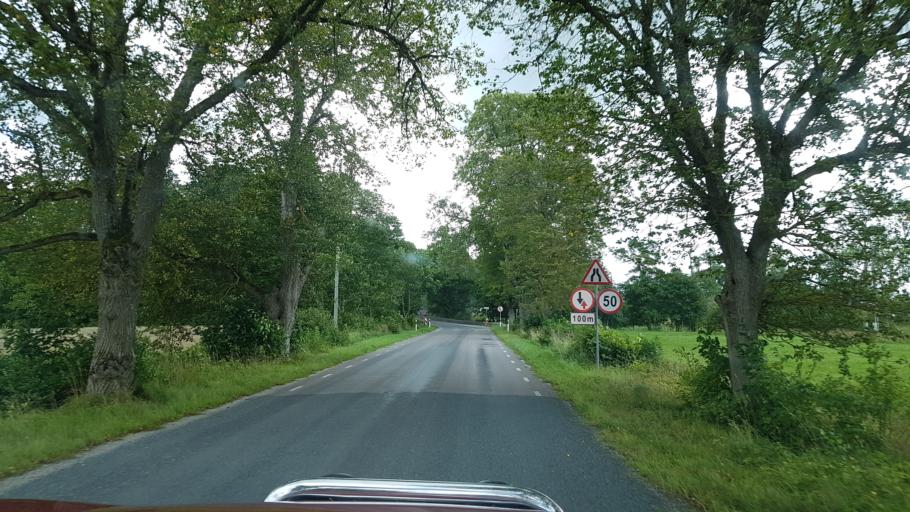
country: EE
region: Laeaene
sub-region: Lihula vald
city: Lihula
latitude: 58.7074
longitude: 24.0226
